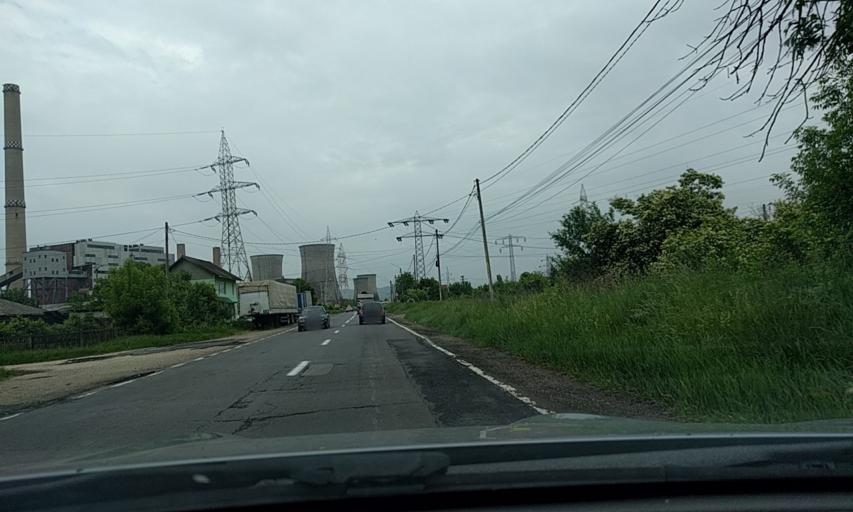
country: RO
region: Dambovita
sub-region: Comuna Doicesti
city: Doicesti
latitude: 44.9974
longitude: 25.4029
